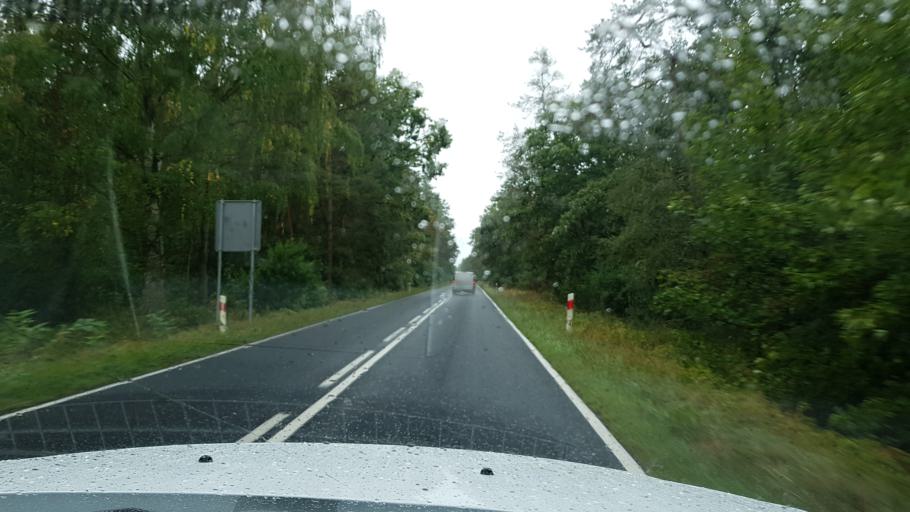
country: DE
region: Brandenburg
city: Schwedt (Oder)
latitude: 53.0521
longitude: 14.3480
